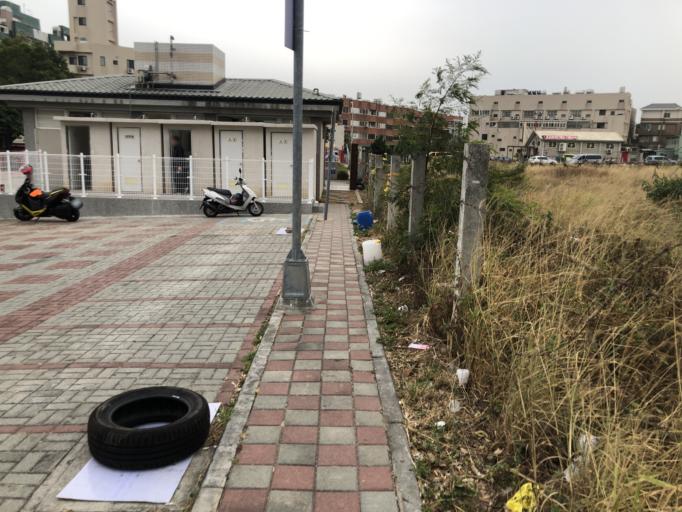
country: TW
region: Taiwan
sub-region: Taichung City
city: Taichung
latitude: 24.1343
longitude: 120.6097
